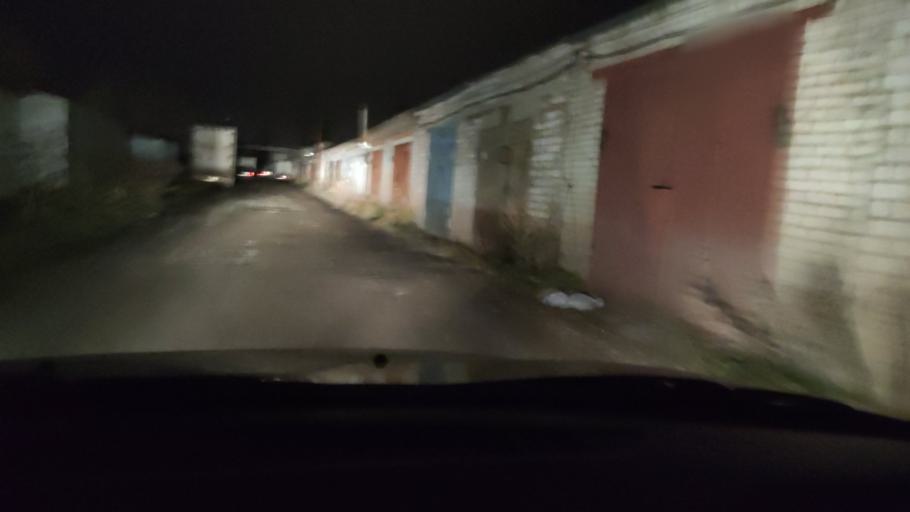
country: RU
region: Perm
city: Kondratovo
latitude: 57.9990
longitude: 56.1149
